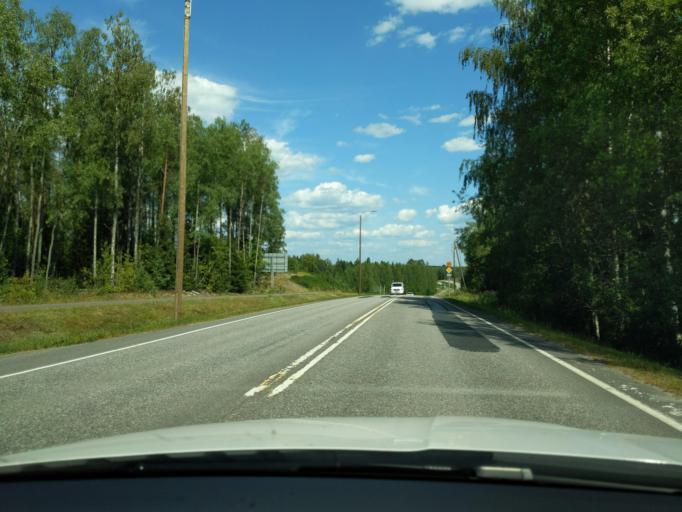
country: FI
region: Paijanne Tavastia
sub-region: Lahti
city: Heinola
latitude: 61.1095
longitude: 25.9371
